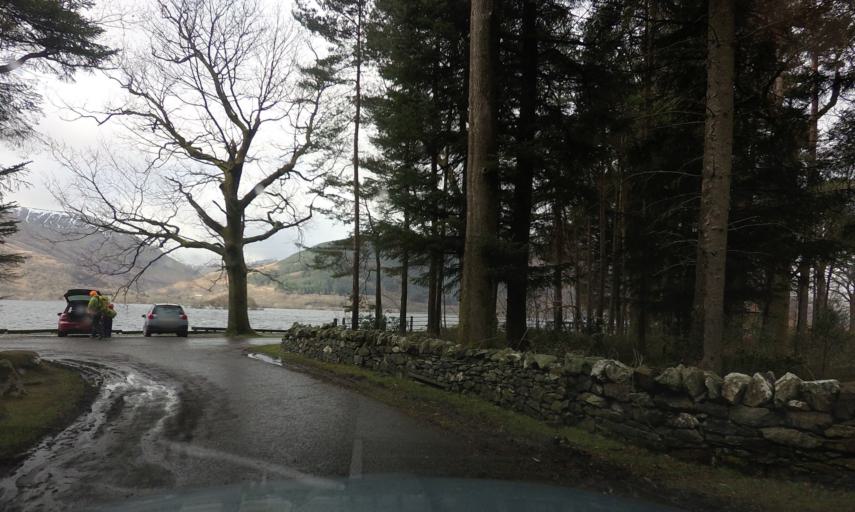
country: GB
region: Scotland
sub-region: West Dunbartonshire
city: Balloch
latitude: 56.1518
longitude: -4.6422
